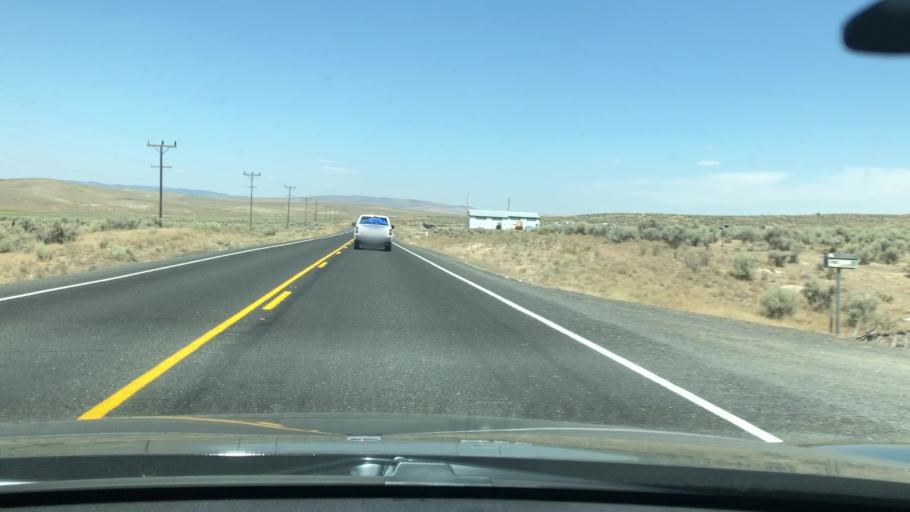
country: US
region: Idaho
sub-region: Owyhee County
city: Murphy
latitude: 42.9994
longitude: -117.0643
